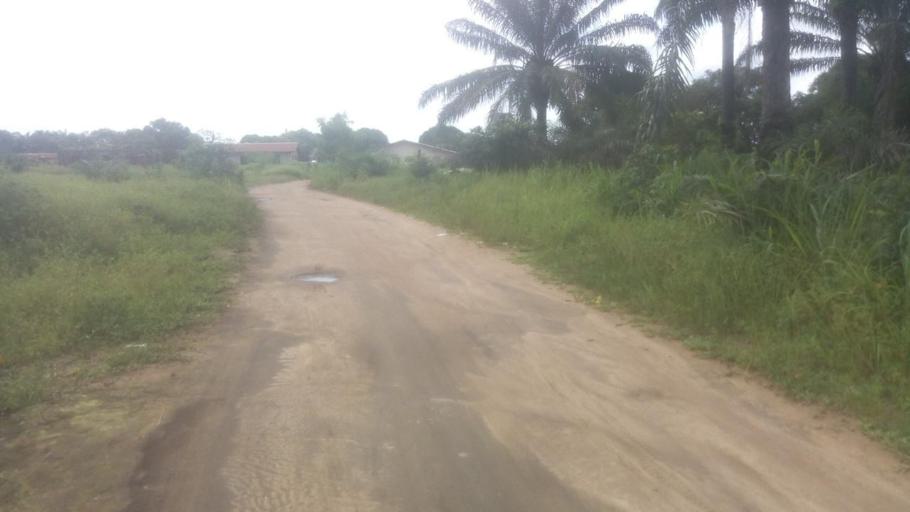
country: SL
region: Northern Province
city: Masoyila
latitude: 8.5966
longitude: -13.1883
